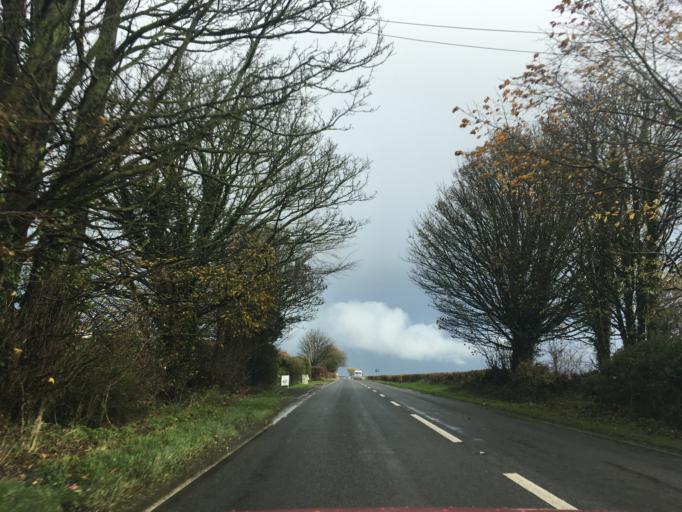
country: GB
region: England
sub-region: South Gloucestershire
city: Cold Ashton
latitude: 51.4558
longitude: -2.3583
